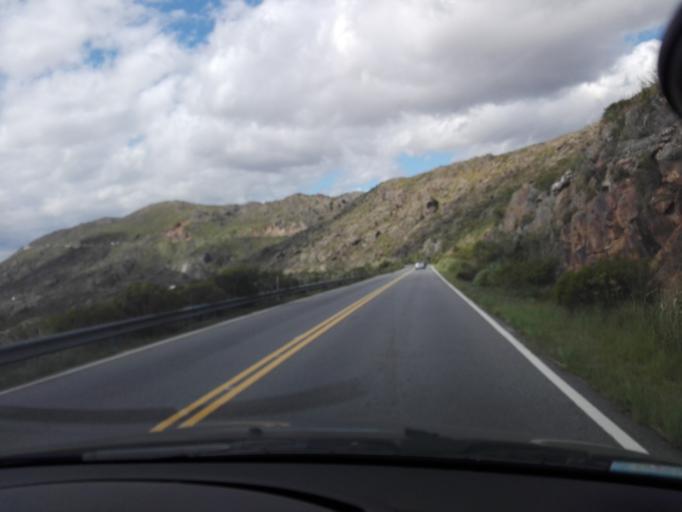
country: AR
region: Cordoba
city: Mina Clavero
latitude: -31.7873
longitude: -64.9123
